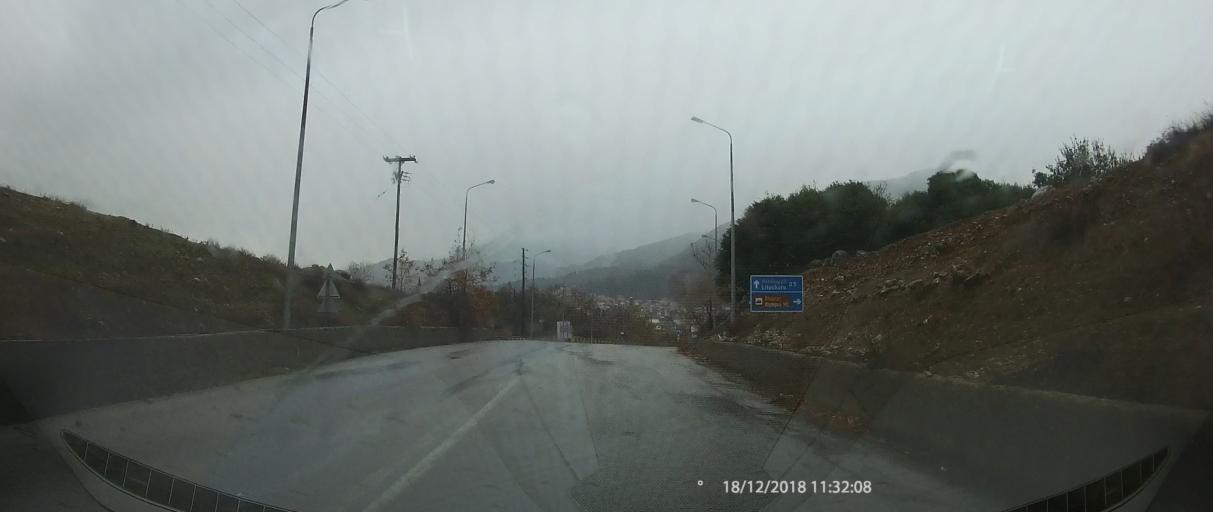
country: GR
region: Central Macedonia
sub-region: Nomos Pierias
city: Litochoro
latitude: 40.1089
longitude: 22.5043
